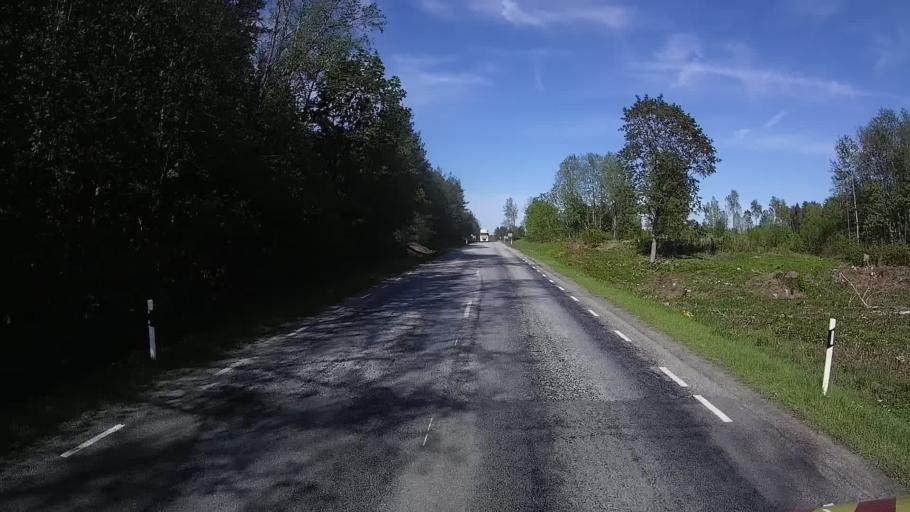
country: EE
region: Vorumaa
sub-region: Antsla vald
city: Vana-Antsla
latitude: 57.9846
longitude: 26.4756
